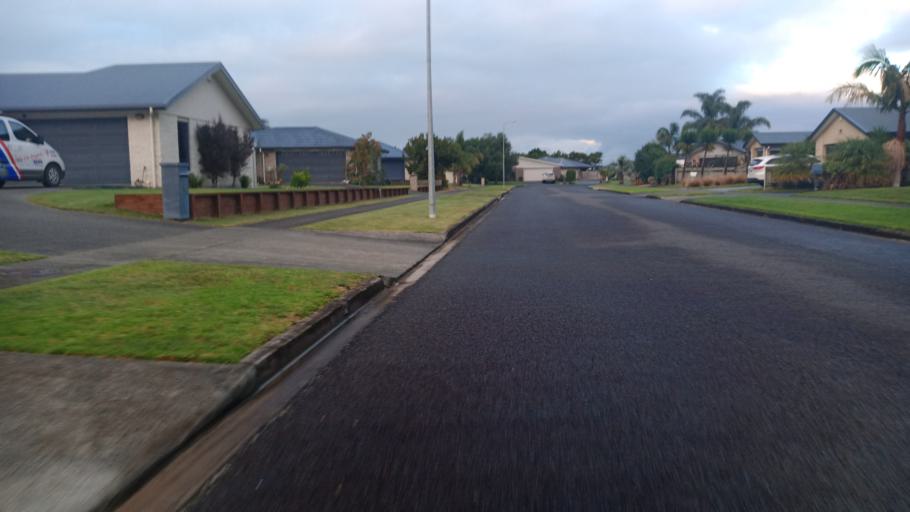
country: NZ
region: Gisborne
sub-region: Gisborne District
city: Gisborne
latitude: -38.6392
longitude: 177.9960
